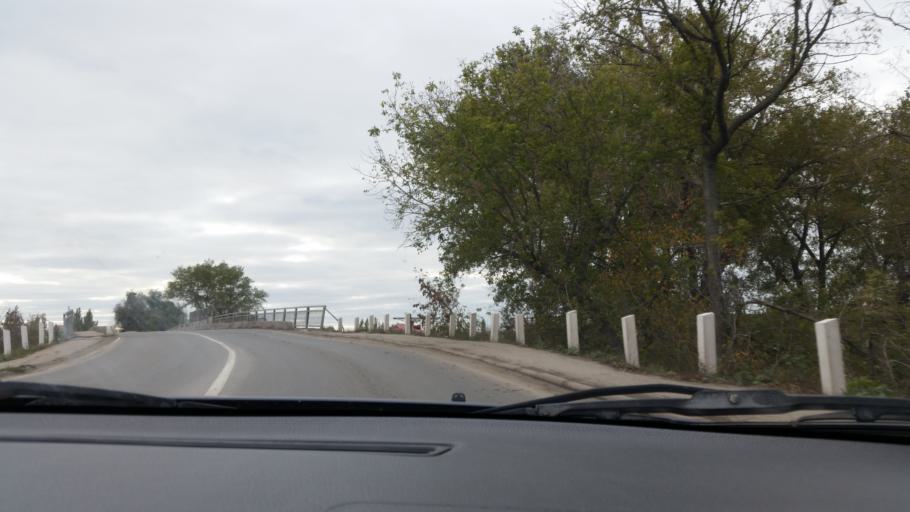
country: RU
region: Lipetsk
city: Gryazi
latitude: 52.4872
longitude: 39.9479
